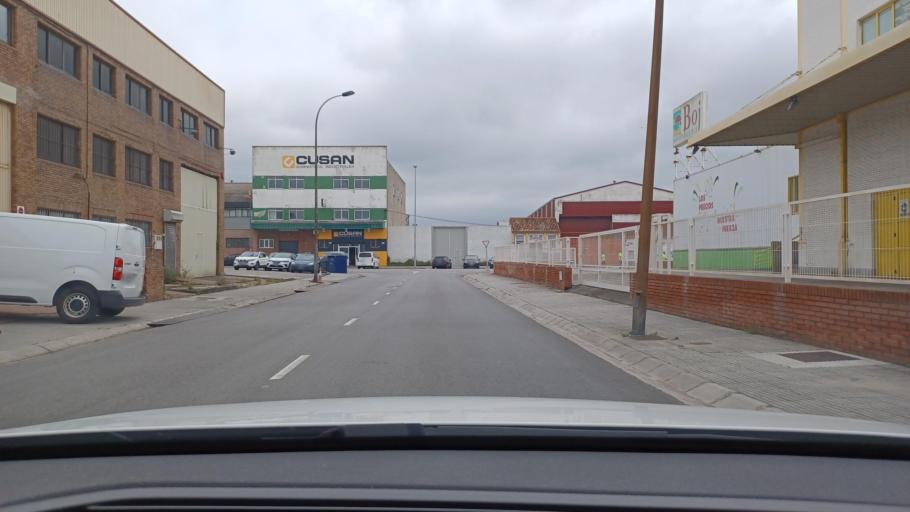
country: ES
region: Asturias
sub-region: Province of Asturias
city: Aviles
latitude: 43.5711
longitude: -5.9244
